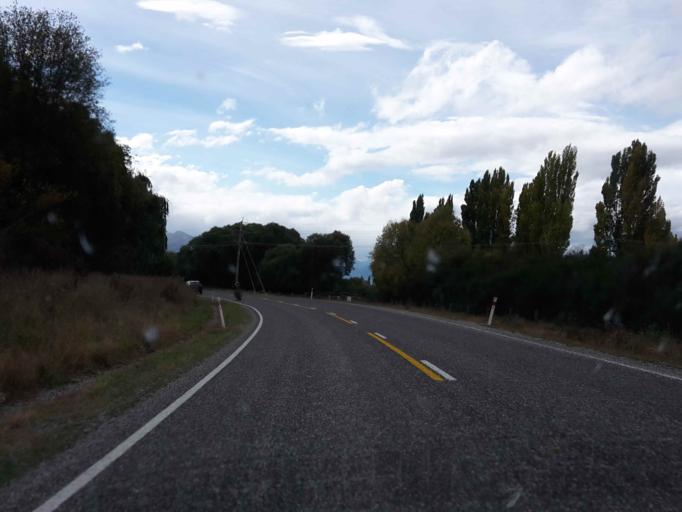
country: NZ
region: Otago
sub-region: Queenstown-Lakes District
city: Wanaka
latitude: -44.7446
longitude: 169.1293
